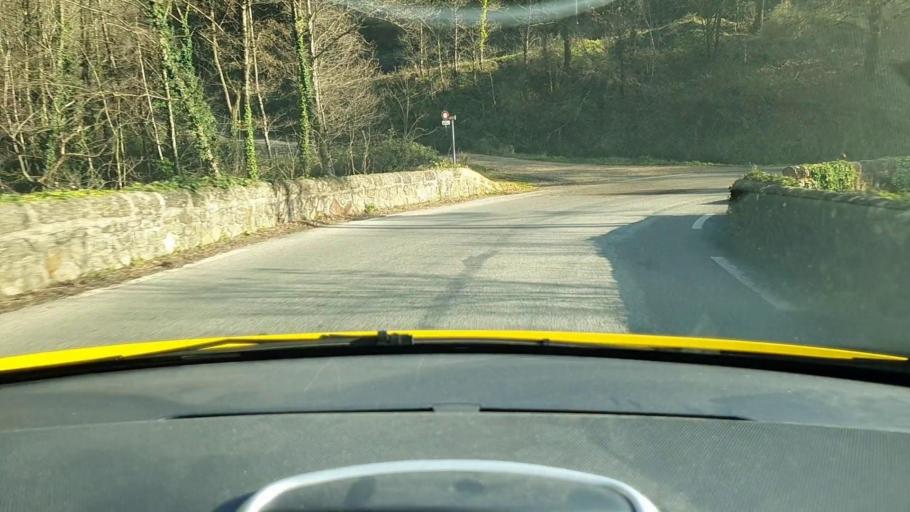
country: FR
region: Languedoc-Roussillon
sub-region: Departement du Gard
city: Branoux-les-Taillades
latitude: 44.3185
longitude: 3.9669
